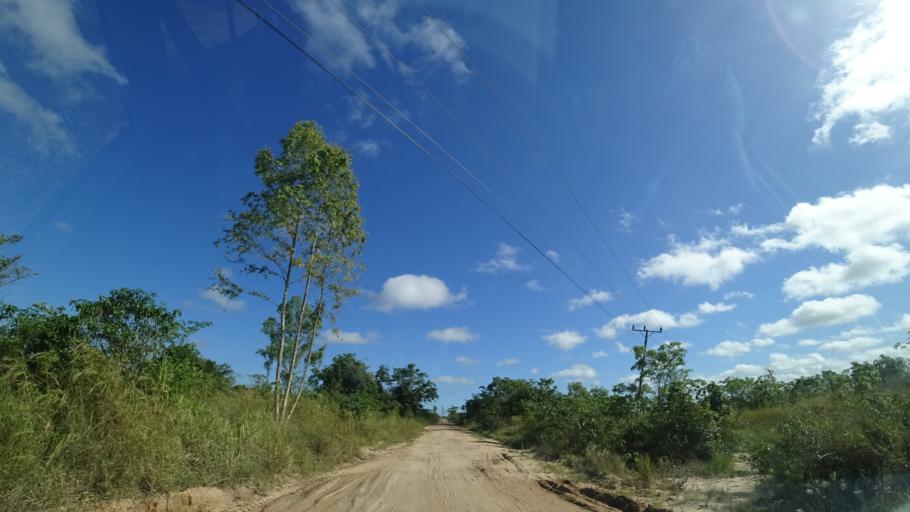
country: MZ
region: Sofala
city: Dondo
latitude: -19.4339
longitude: 34.7123
